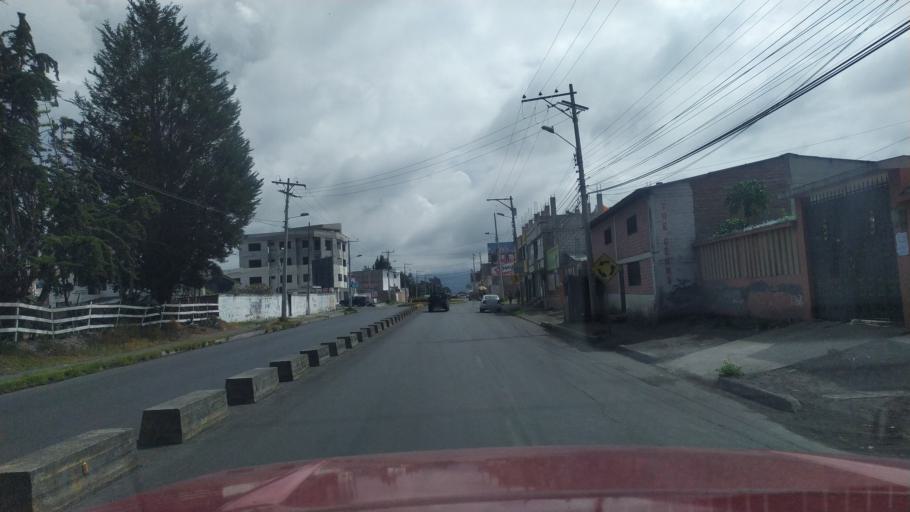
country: EC
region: Chimborazo
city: Riobamba
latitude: -1.6507
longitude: -78.6431
